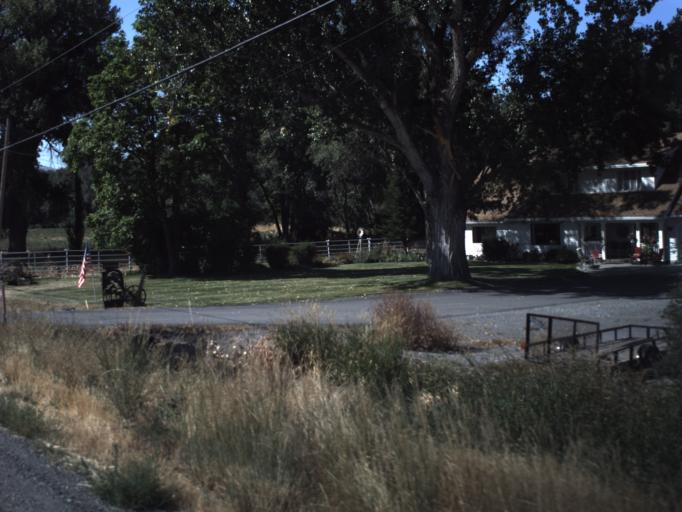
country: US
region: Utah
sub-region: Cache County
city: Hyrum
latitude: 41.5969
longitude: -111.8352
